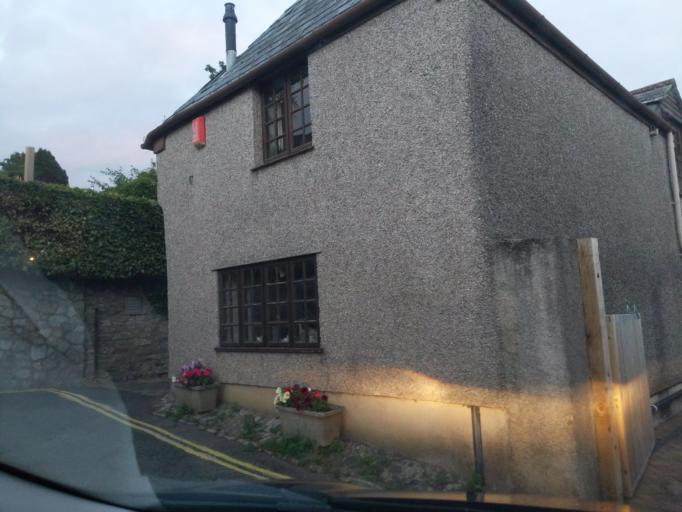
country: GB
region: England
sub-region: Plymouth
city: Plymstock
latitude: 50.3544
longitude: -4.1117
